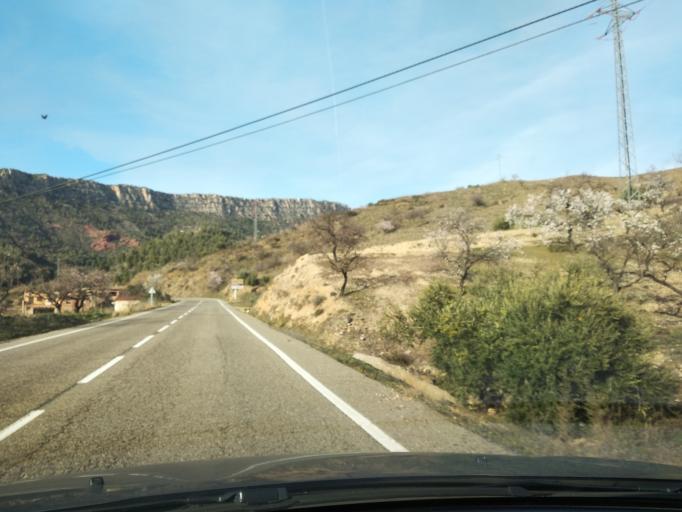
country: ES
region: Catalonia
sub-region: Provincia de Tarragona
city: Margalef
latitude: 41.2181
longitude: 0.7651
